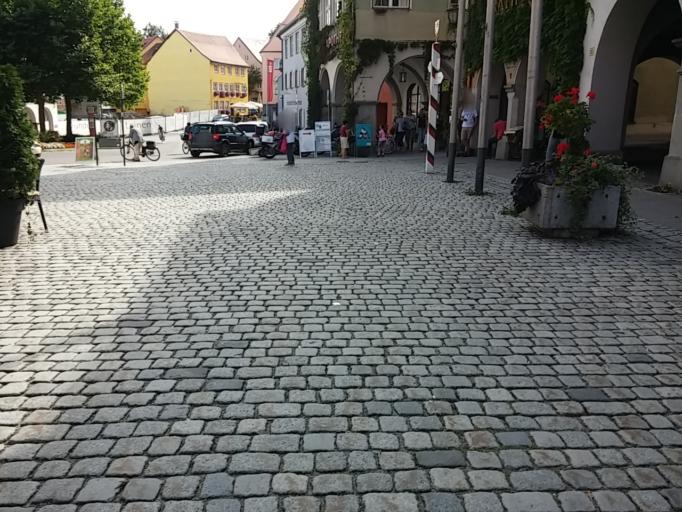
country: DE
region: Baden-Wuerttemberg
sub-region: Tuebingen Region
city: Isny im Allgau
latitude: 47.6925
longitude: 10.0396
